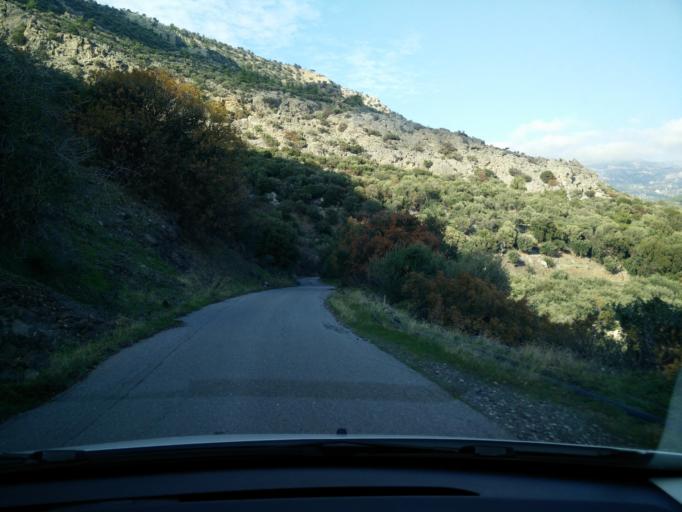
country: GR
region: Crete
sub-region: Nomos Lasithiou
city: Gra Liyia
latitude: 35.0366
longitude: 25.5711
